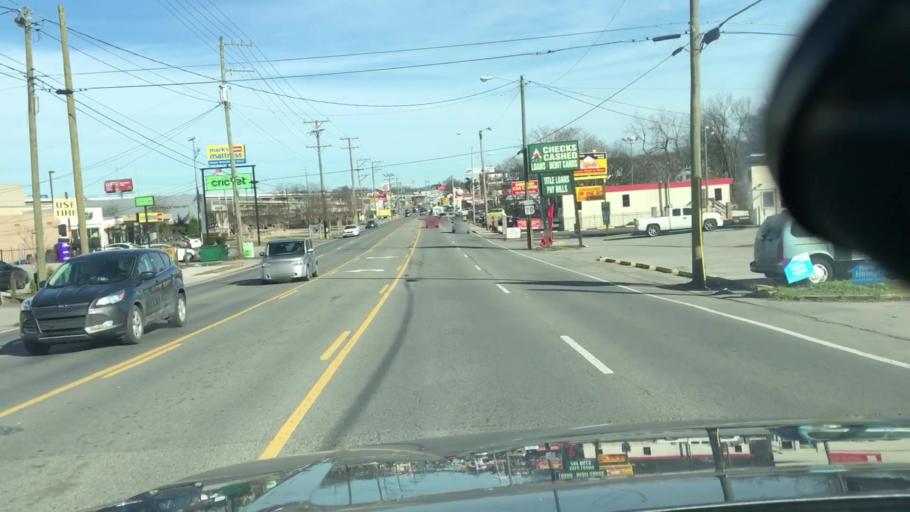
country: US
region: Tennessee
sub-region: Davidson County
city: Belle Meade
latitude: 36.1505
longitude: -86.8566
